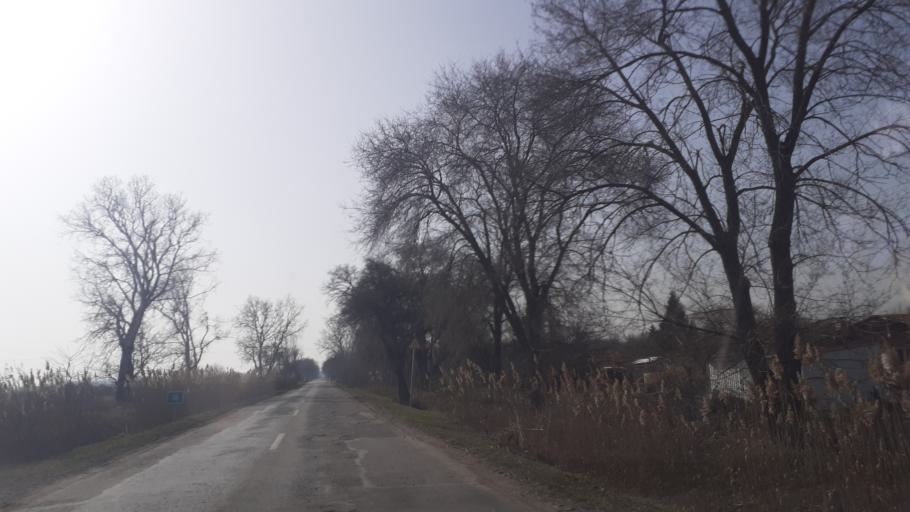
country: HU
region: Bacs-Kiskun
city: Kunszentmiklos
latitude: 47.0646
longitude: 19.2535
